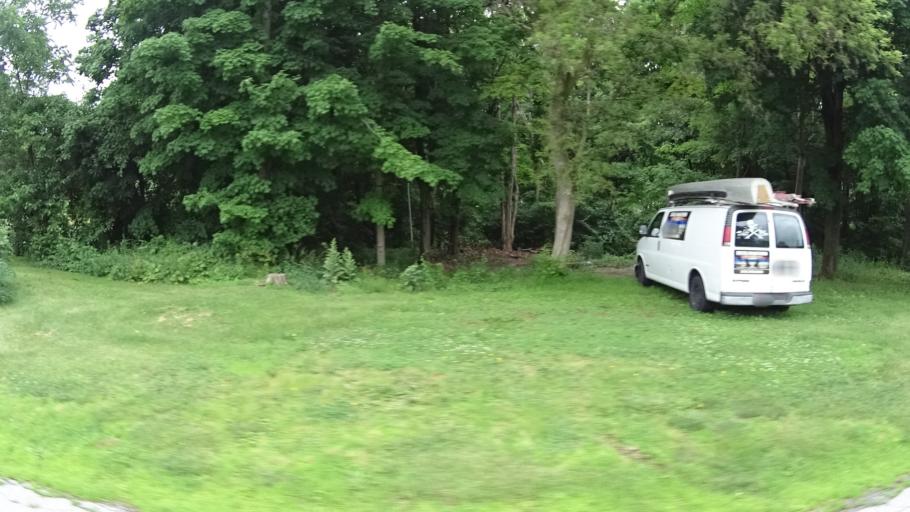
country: US
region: Ohio
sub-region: Erie County
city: Milan
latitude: 41.2985
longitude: -82.5845
